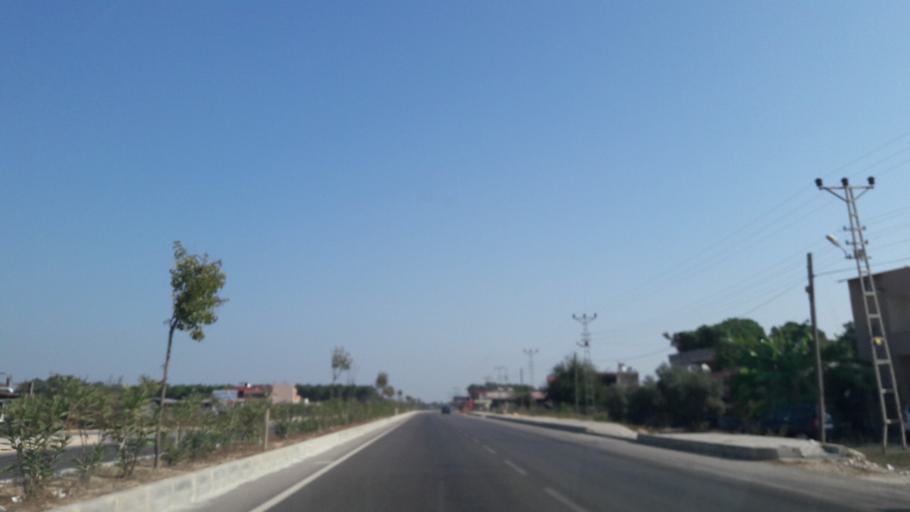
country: TR
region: Adana
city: Yakapinar
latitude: 37.1147
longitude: 35.5129
